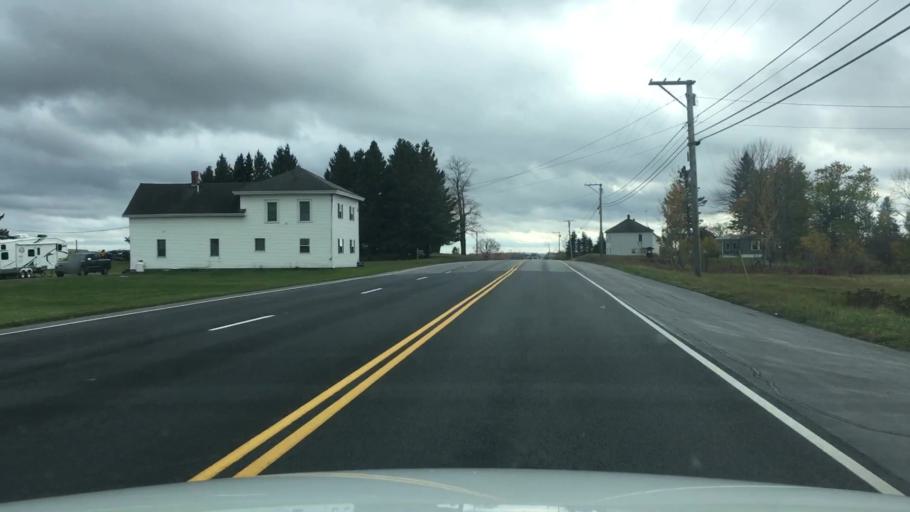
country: US
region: Maine
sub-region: Aroostook County
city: Houlton
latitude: 46.2229
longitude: -67.8411
